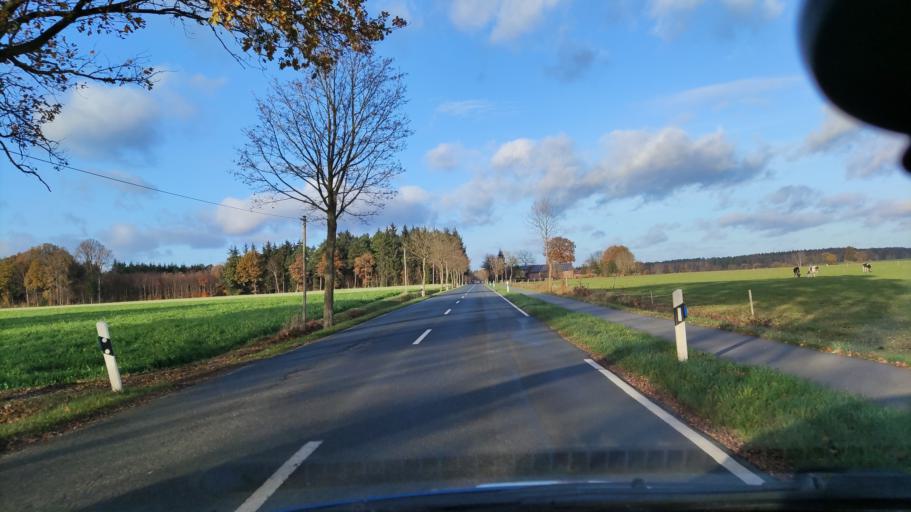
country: DE
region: Lower Saxony
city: Soltau
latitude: 53.0404
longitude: 9.8292
